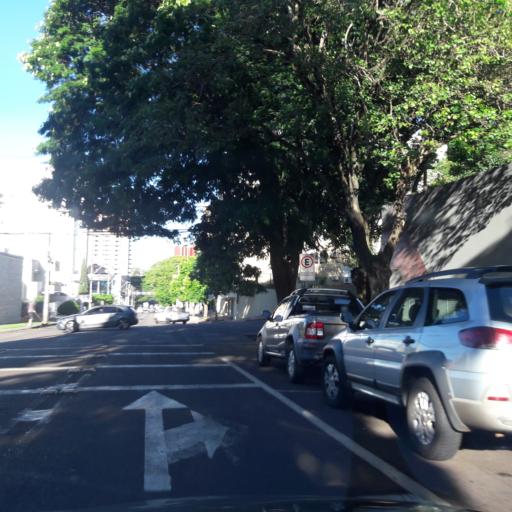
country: BR
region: Parana
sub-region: Cascavel
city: Cascavel
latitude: -24.9495
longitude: -53.4515
